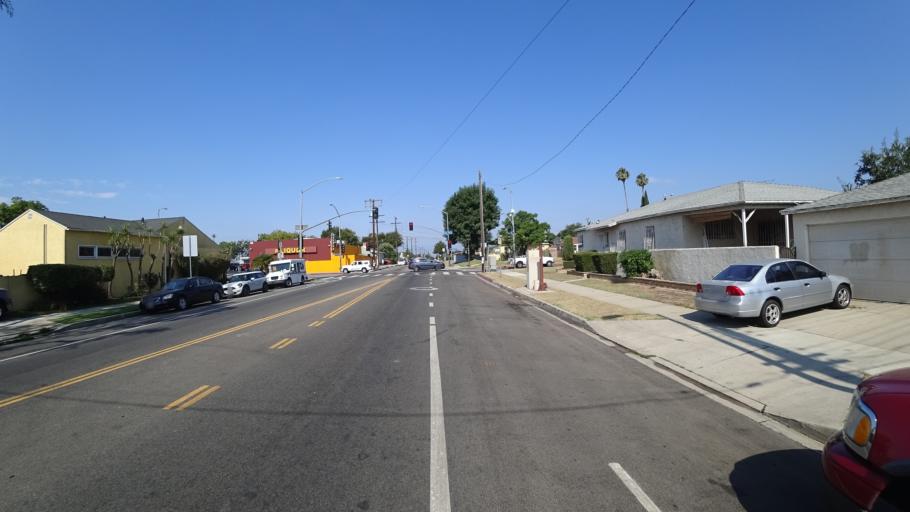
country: US
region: California
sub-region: Los Angeles County
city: Westmont
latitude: 33.9528
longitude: -118.3172
